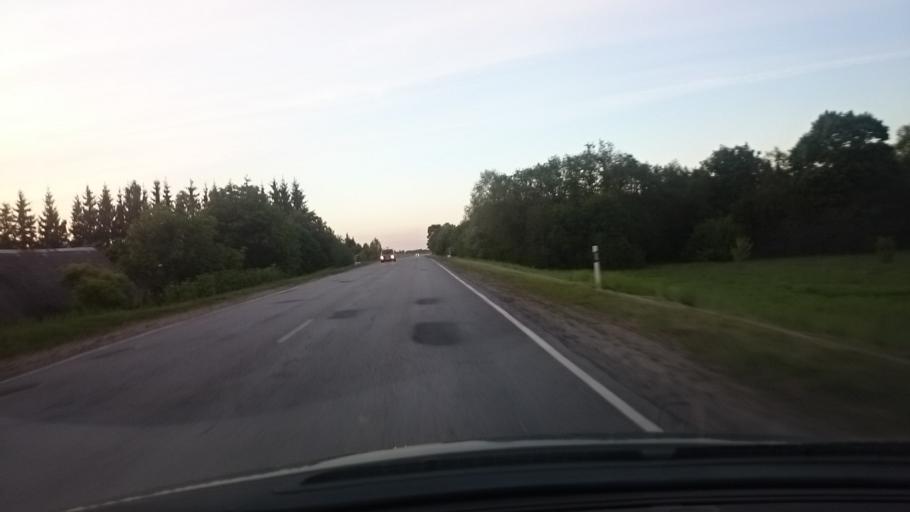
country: EE
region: Viljandimaa
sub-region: Vohma linn
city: Vohma
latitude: 58.6365
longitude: 25.5745
